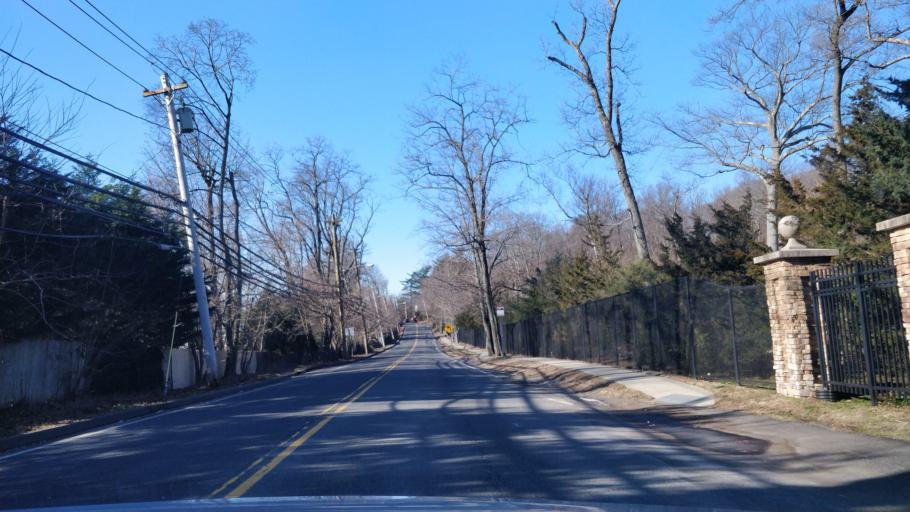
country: US
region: New York
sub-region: Nassau County
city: East Hills
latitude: 40.7948
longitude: -73.6288
